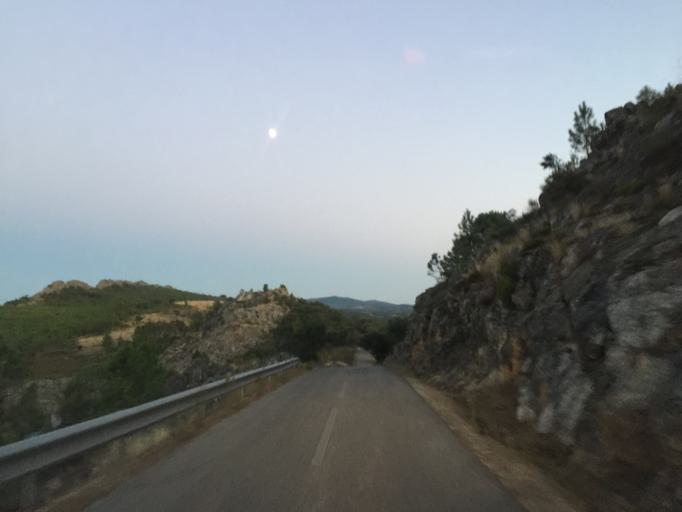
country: PT
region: Portalegre
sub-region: Castelo de Vide
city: Castelo de Vide
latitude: 39.4026
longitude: -7.4536
